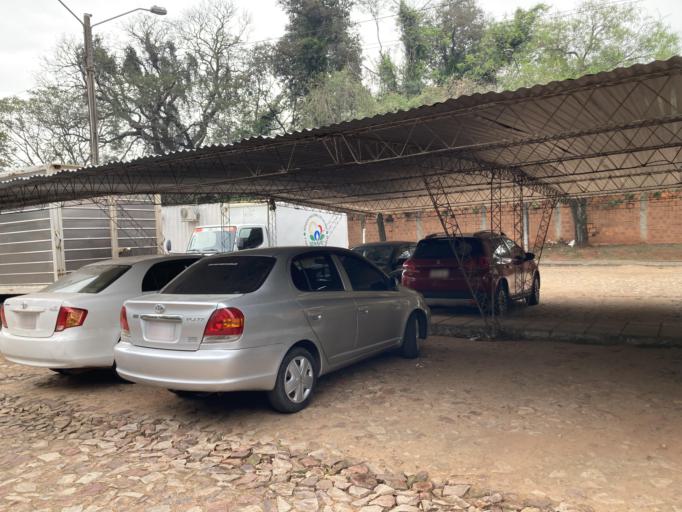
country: PY
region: Central
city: Fernando de la Mora
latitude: -25.3461
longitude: -57.5293
